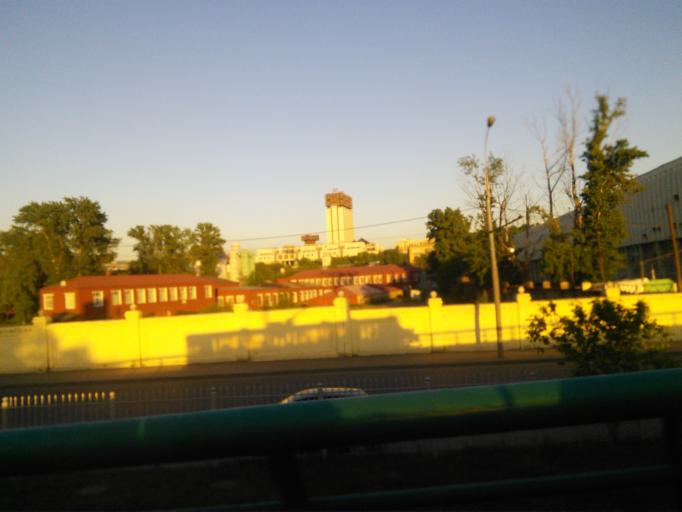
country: RU
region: Moscow
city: Luzhniki
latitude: 55.7155
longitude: 37.5665
